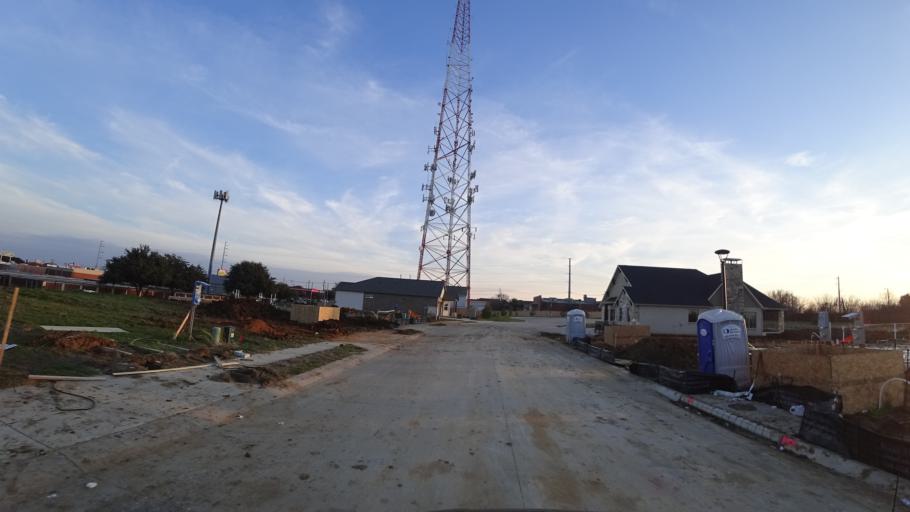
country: US
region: Texas
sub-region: Denton County
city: Lewisville
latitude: 33.0064
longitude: -96.9833
